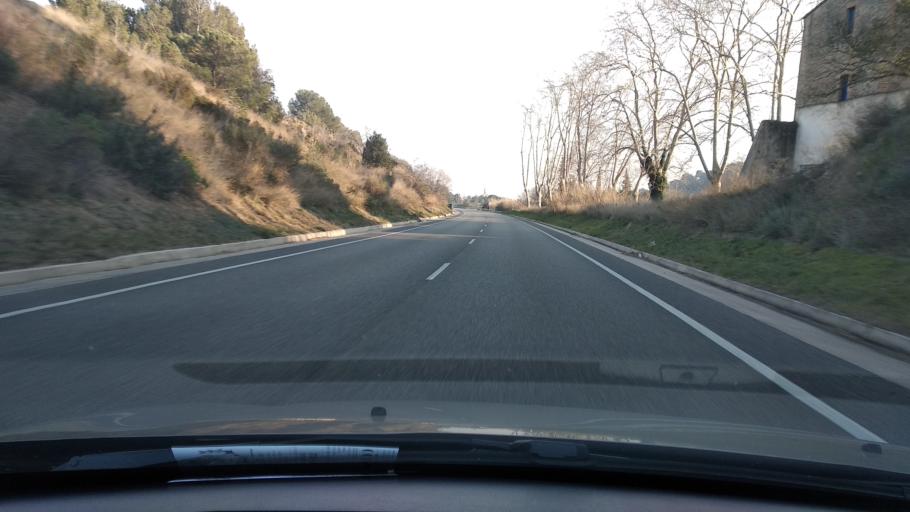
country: ES
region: Catalonia
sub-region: Provincia de Tarragona
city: les Borges del Camp
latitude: 41.1873
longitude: 1.0032
